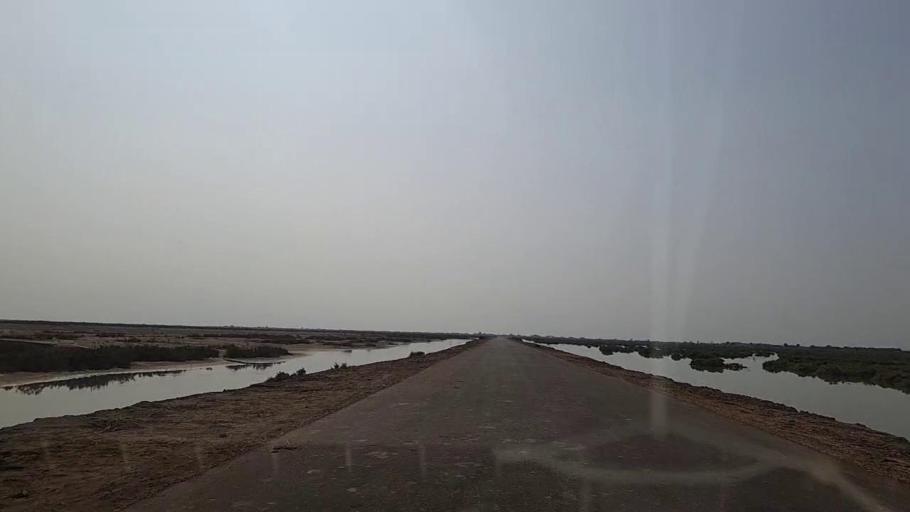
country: PK
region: Sindh
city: Chuhar Jamali
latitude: 24.2133
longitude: 67.8637
